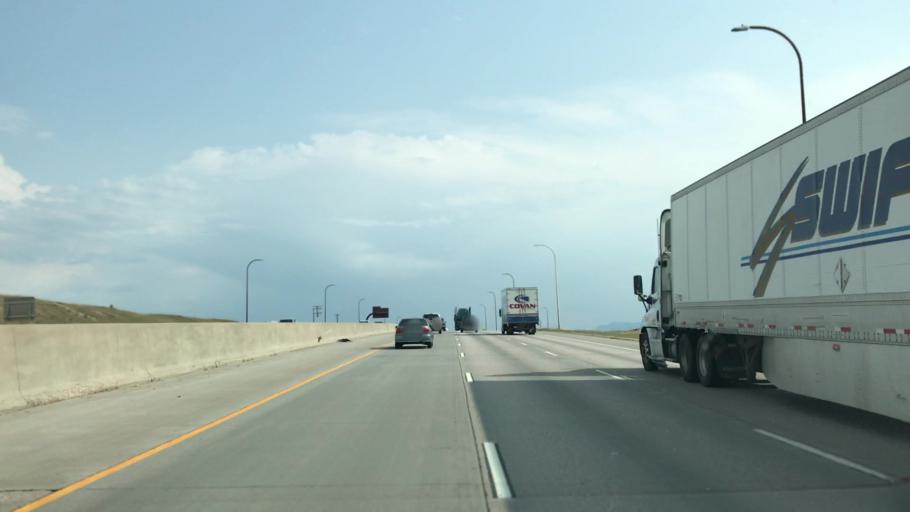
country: US
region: Colorado
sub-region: El Paso County
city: Monument
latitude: 39.0878
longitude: -104.8617
